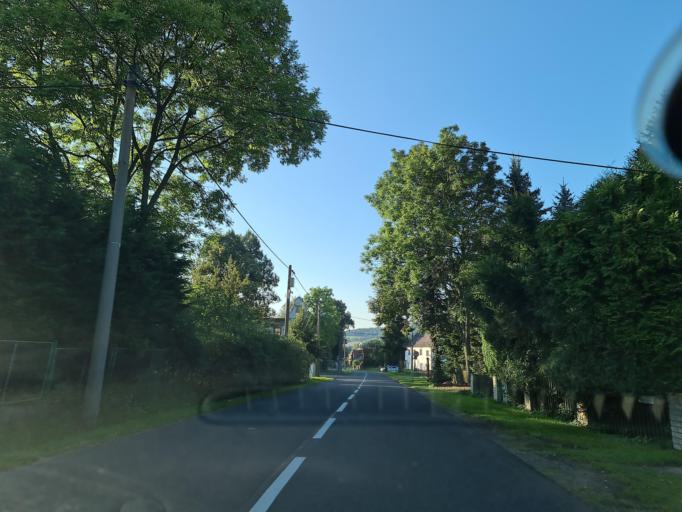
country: DE
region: Saxony
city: Olbernhau
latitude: 50.6383
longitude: 13.3840
